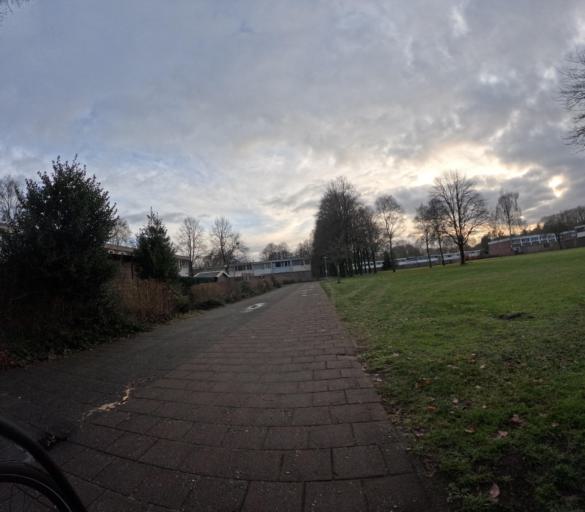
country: NL
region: Drenthe
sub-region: Gemeente Emmen
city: Emmen
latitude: 52.7888
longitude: 6.9338
